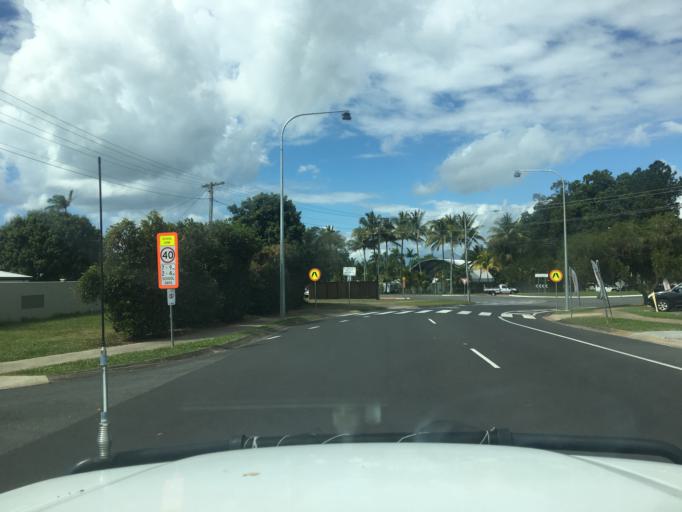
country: AU
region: Queensland
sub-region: Cairns
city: Woree
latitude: -16.9666
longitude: 145.7413
